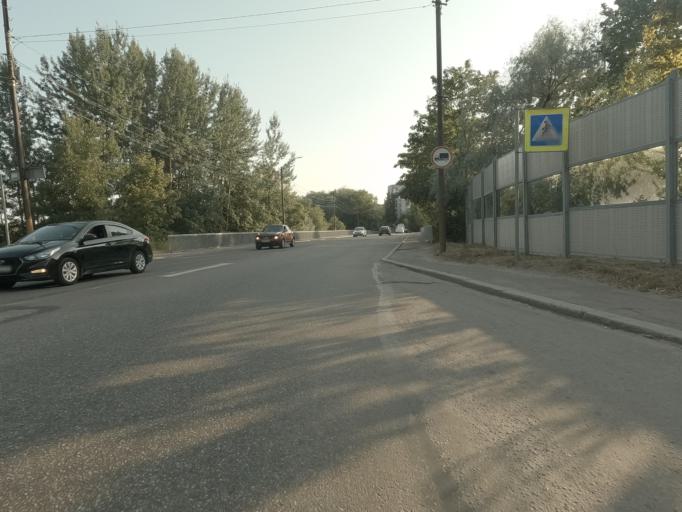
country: RU
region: Leningrad
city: Vyborg
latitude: 60.7208
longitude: 28.7670
